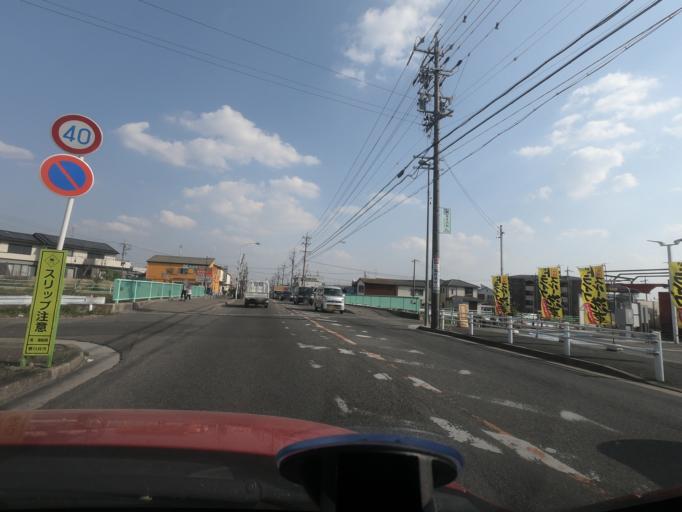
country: JP
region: Aichi
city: Kasugai
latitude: 35.2492
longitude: 136.9592
